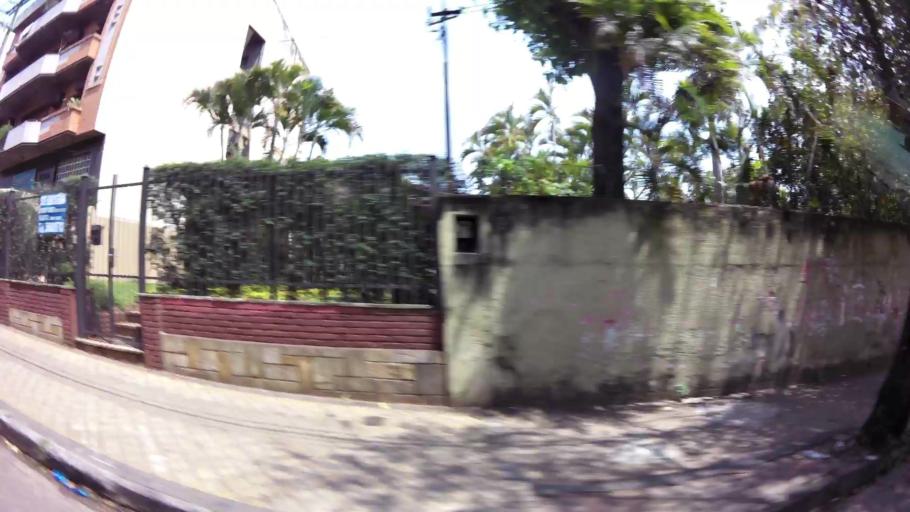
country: PY
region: Central
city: Lambare
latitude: -25.3110
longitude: -57.5971
